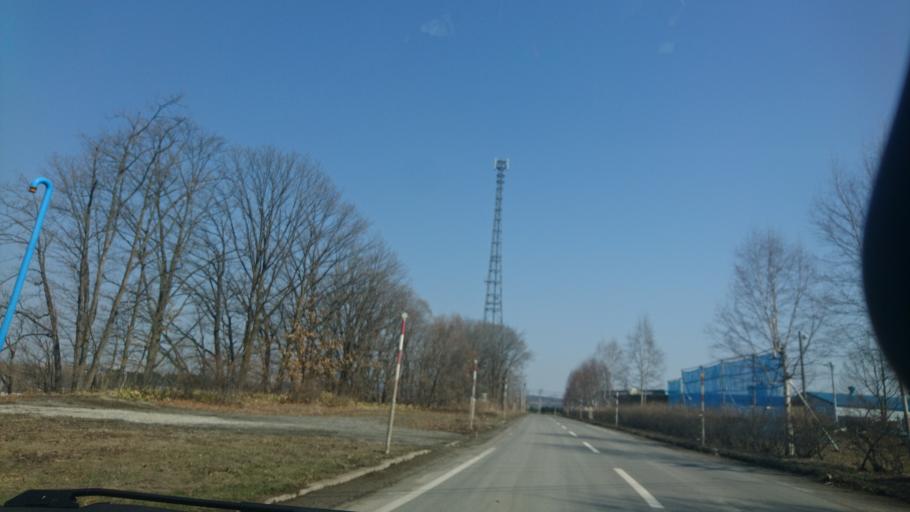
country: JP
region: Hokkaido
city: Obihiro
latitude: 42.9199
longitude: 143.0718
